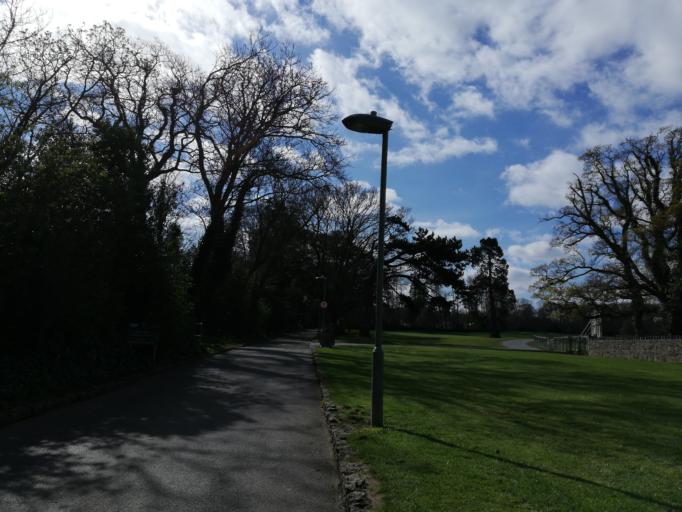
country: IE
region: Leinster
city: Malahide
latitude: 53.4492
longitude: -6.1587
